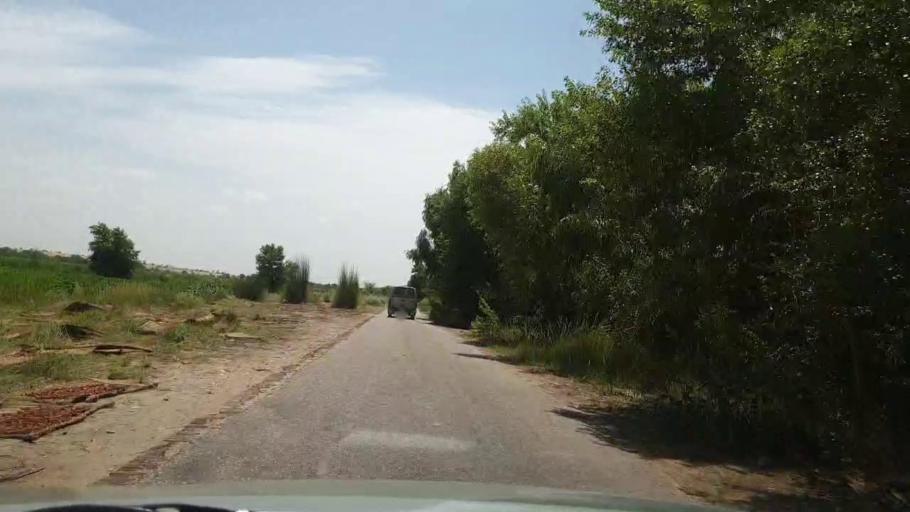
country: PK
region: Sindh
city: Bozdar
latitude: 27.0716
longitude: 68.9764
